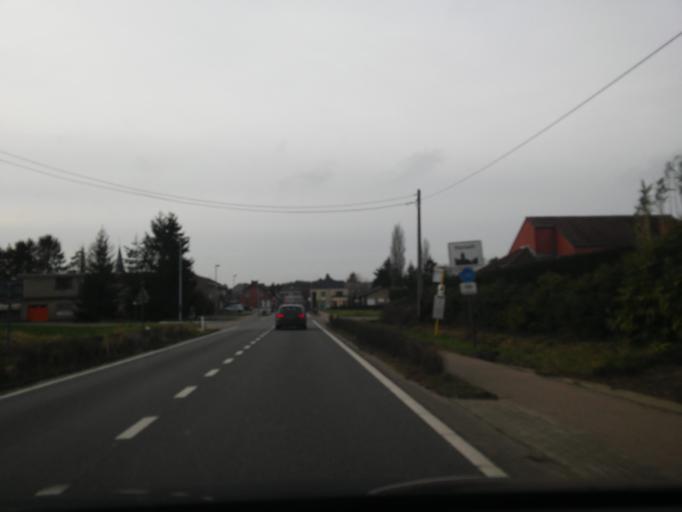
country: BE
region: Flanders
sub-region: Provincie Antwerpen
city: Herselt
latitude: 51.0525
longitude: 4.8875
